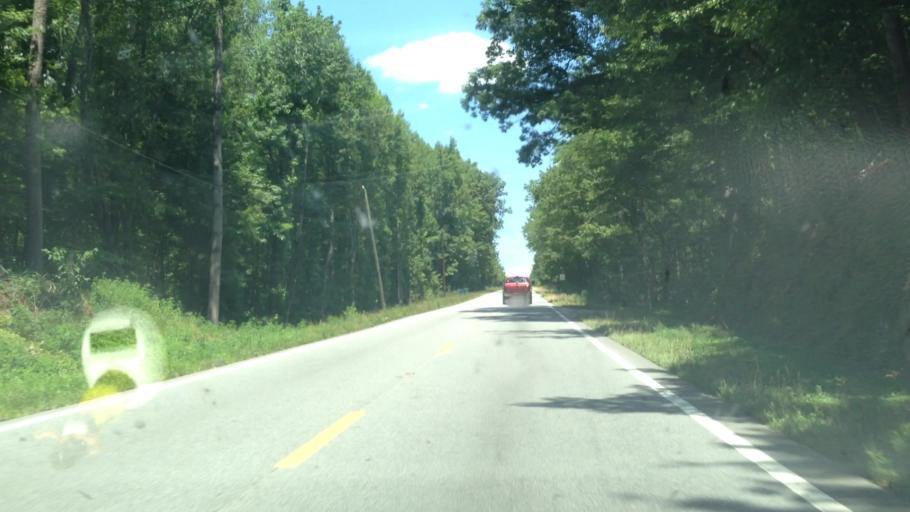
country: US
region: North Carolina
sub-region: Guilford County
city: Stokesdale
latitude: 36.2645
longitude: -79.9525
